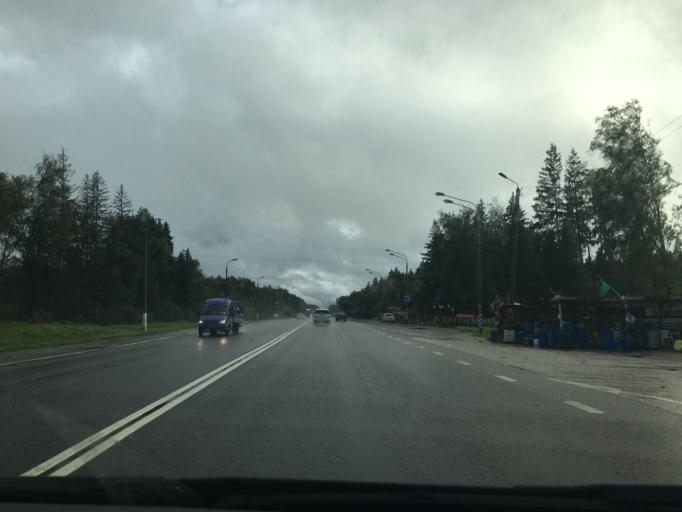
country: RU
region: Kaluga
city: Balabanovo
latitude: 55.1629
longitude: 36.6681
